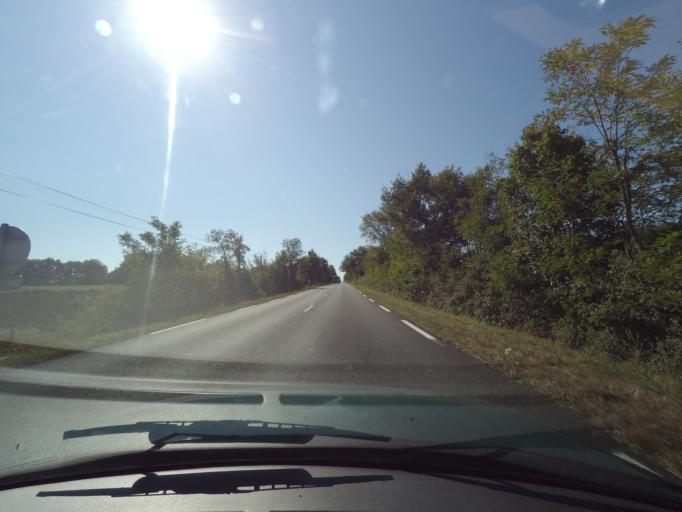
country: FR
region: Poitou-Charentes
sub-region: Departement de la Vienne
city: Saulge
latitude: 46.3454
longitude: 0.7940
